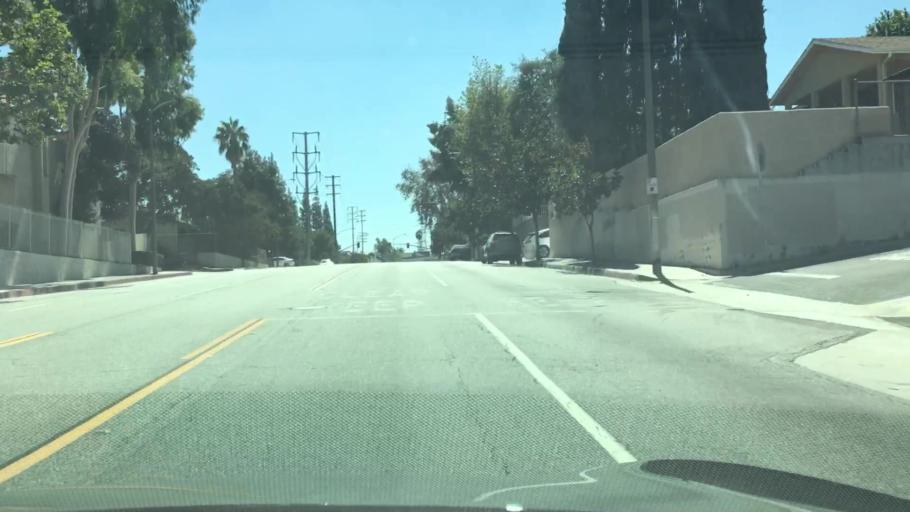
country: US
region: California
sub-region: Los Angeles County
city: South San Gabriel
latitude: 34.0433
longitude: -118.0819
